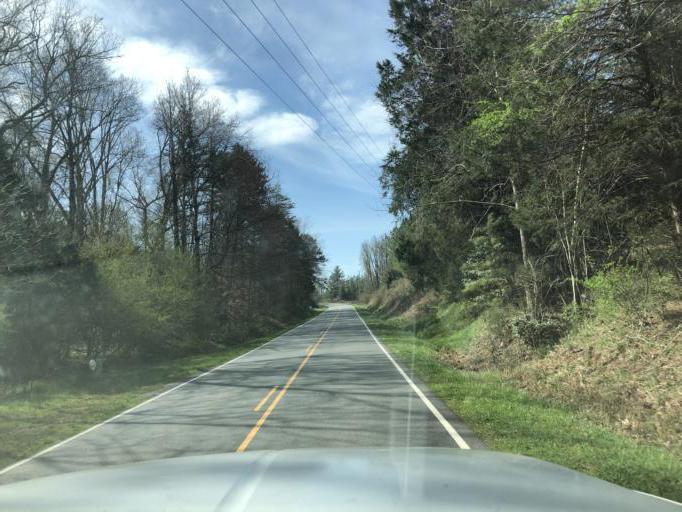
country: US
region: North Carolina
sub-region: Cleveland County
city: Shelby
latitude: 35.4429
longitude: -81.6438
